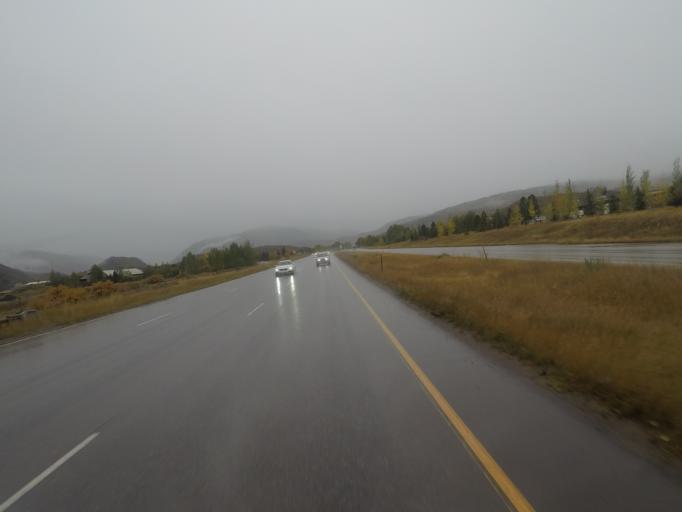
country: US
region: Colorado
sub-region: Pitkin County
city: Aspen
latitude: 39.2276
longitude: -106.8675
